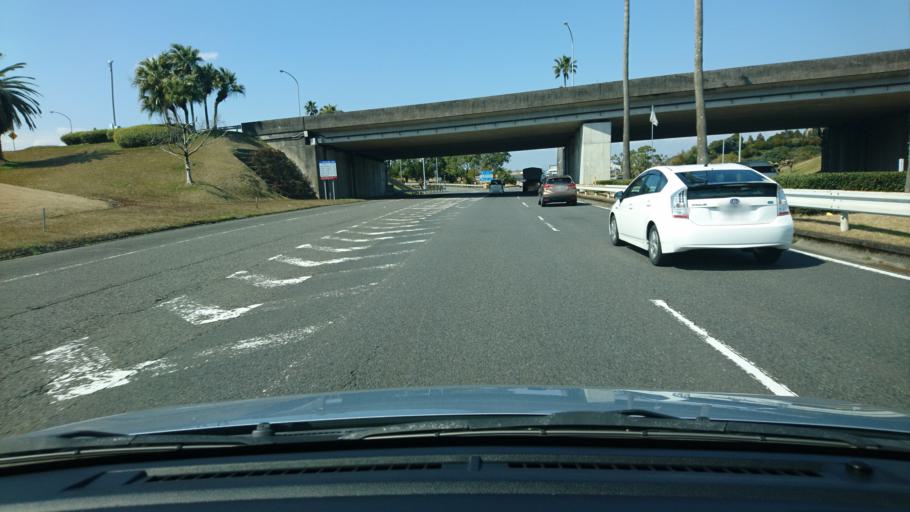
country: JP
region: Miyazaki
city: Miyazaki-shi
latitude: 31.8702
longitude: 131.4165
